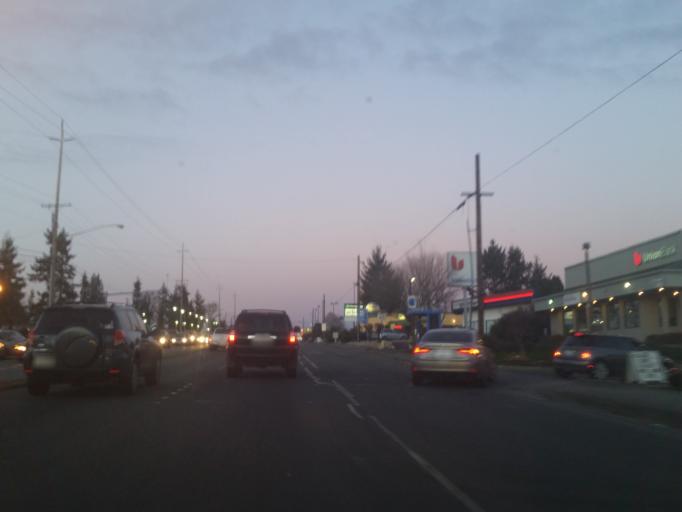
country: US
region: Washington
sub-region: Snohomish County
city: Lynnwood
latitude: 47.8071
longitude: -122.3263
